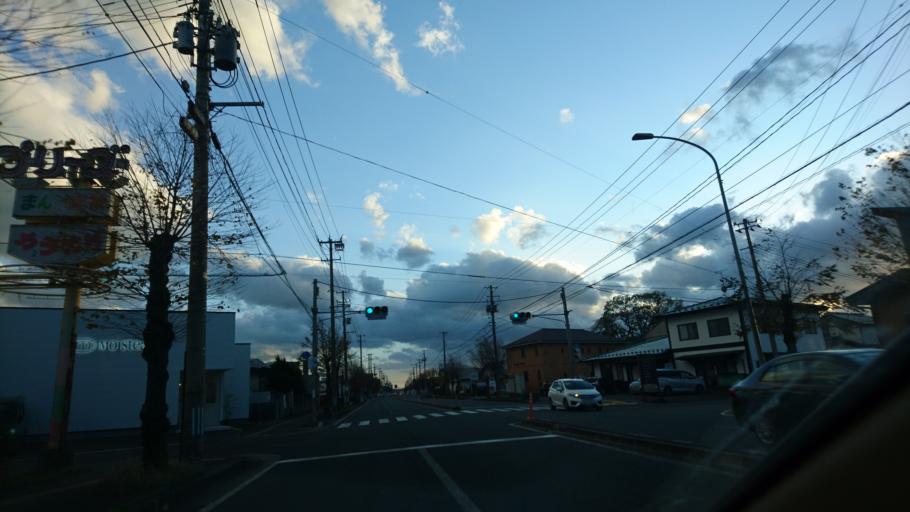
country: JP
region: Iwate
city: Mizusawa
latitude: 39.1489
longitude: 141.1319
